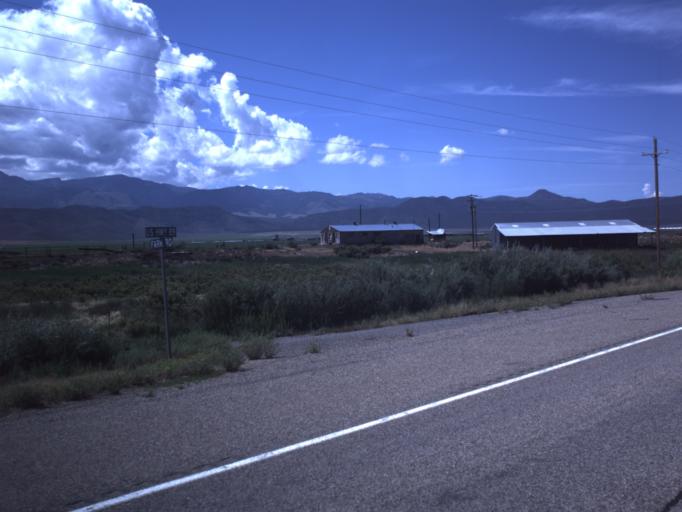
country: US
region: Utah
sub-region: Piute County
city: Junction
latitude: 38.1869
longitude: -112.2412
